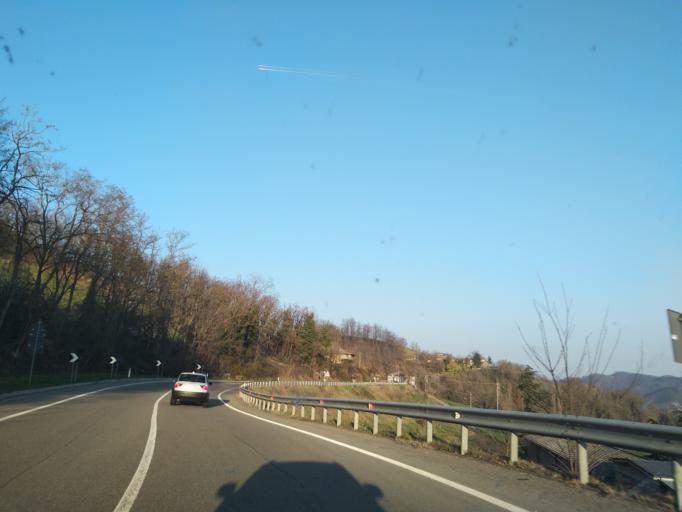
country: IT
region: Emilia-Romagna
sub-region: Provincia di Reggio Emilia
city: Felina
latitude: 44.4617
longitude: 10.4775
